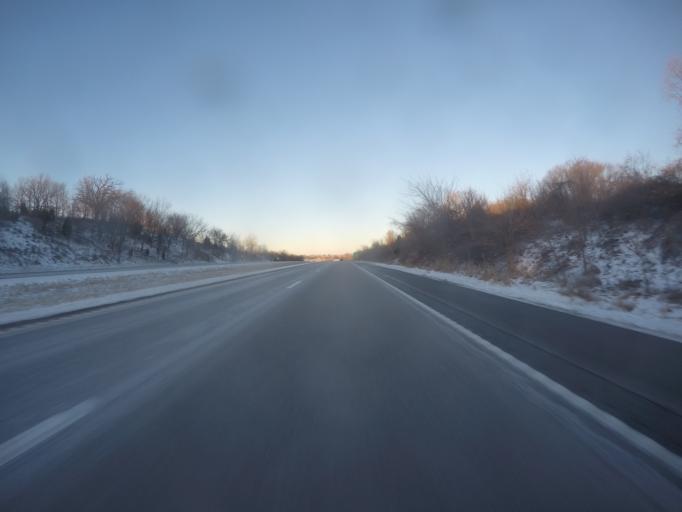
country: US
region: Missouri
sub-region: Platte County
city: Platte City
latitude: 39.3035
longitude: -94.7606
